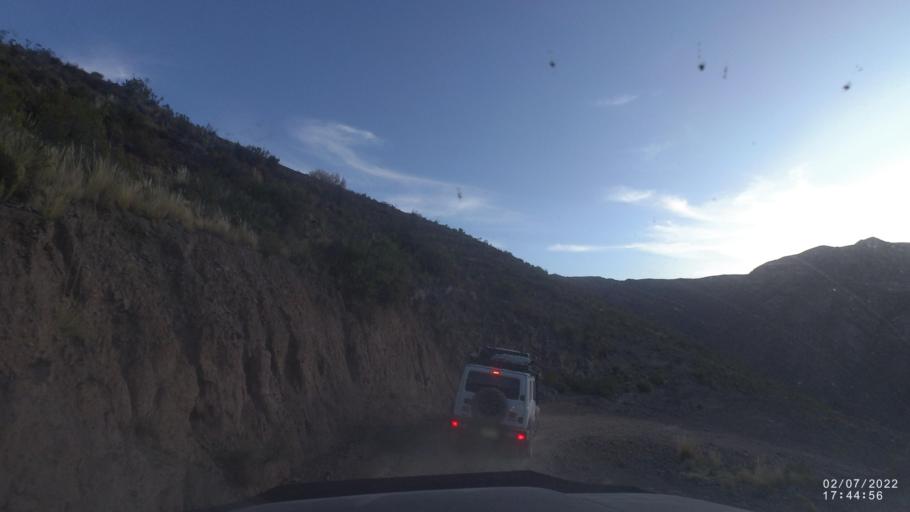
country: BO
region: Cochabamba
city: Irpa Irpa
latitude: -17.8536
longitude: -66.6209
